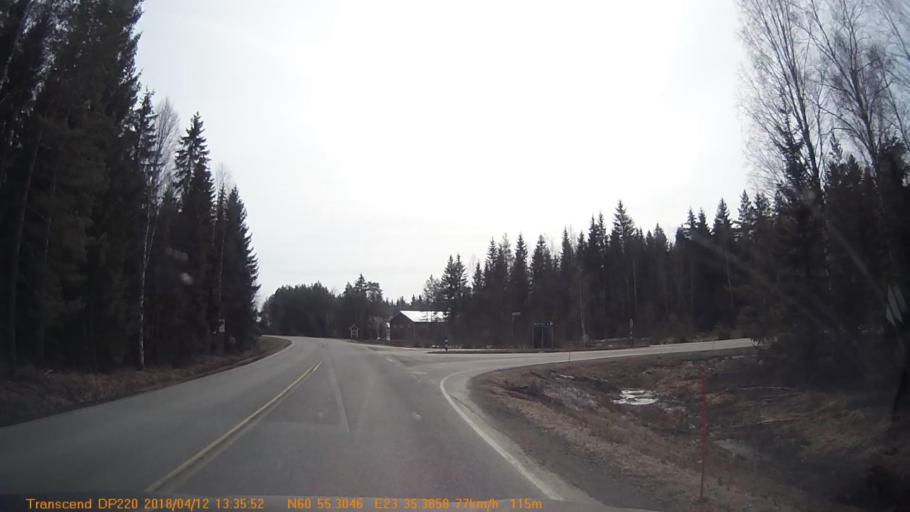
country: FI
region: Haeme
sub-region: Forssa
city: Forssa
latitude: 60.9215
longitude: 23.5897
